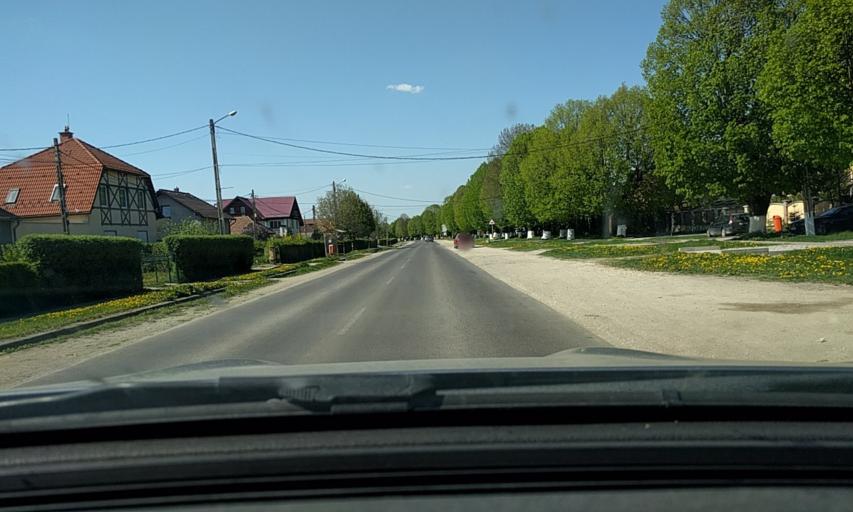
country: RO
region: Brasov
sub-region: Comuna Harman
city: Harman
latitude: 45.7057
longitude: 25.6878
